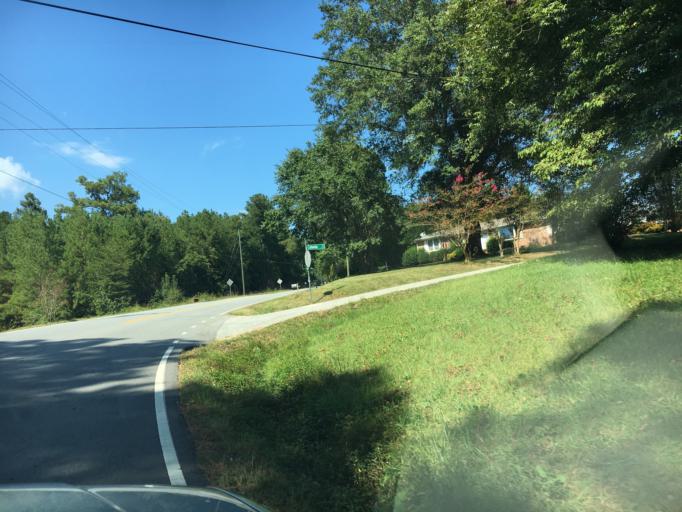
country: US
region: South Carolina
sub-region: Oconee County
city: Utica
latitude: 34.7011
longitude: -82.9280
